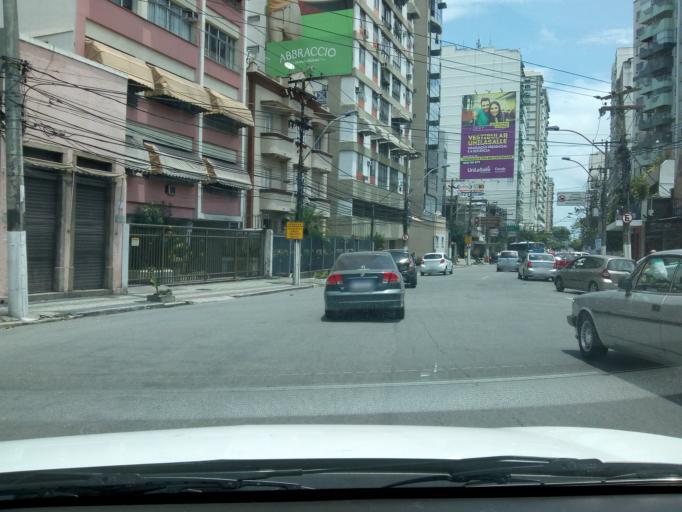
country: BR
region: Rio de Janeiro
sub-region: Niteroi
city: Niteroi
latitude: -22.9001
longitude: -43.1123
